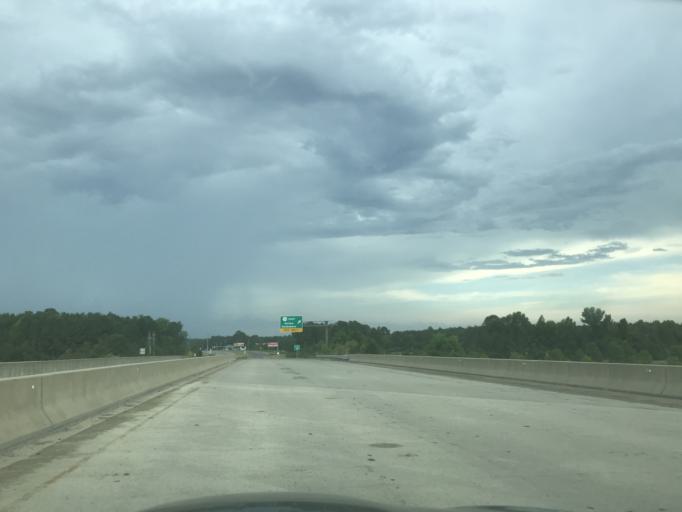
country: US
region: North Carolina
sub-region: Johnston County
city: Wilsons Mills
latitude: 35.5982
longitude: -78.4117
